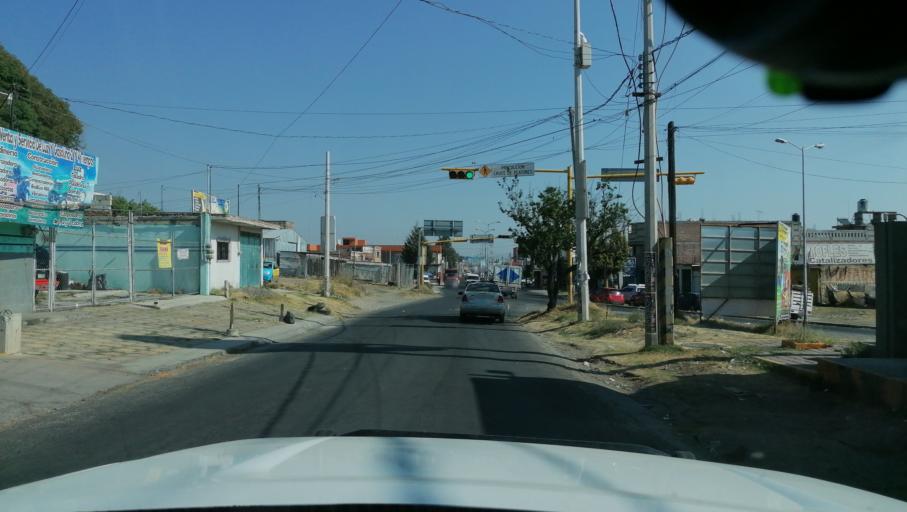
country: MX
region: Puebla
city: Huejotzingo
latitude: 19.1500
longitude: -98.4074
